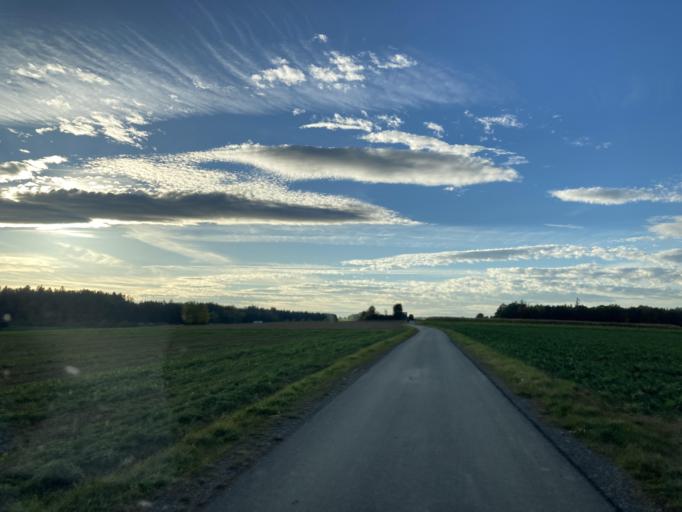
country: DE
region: Baden-Wuerttemberg
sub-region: Regierungsbezirk Stuttgart
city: Motzingen
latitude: 48.5211
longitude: 8.7849
